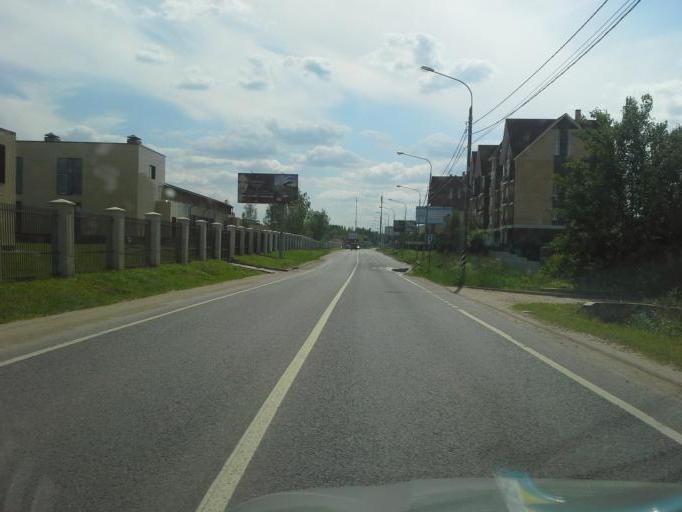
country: RU
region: Moskovskaya
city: Gorki Vtoryye
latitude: 55.7008
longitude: 37.1544
